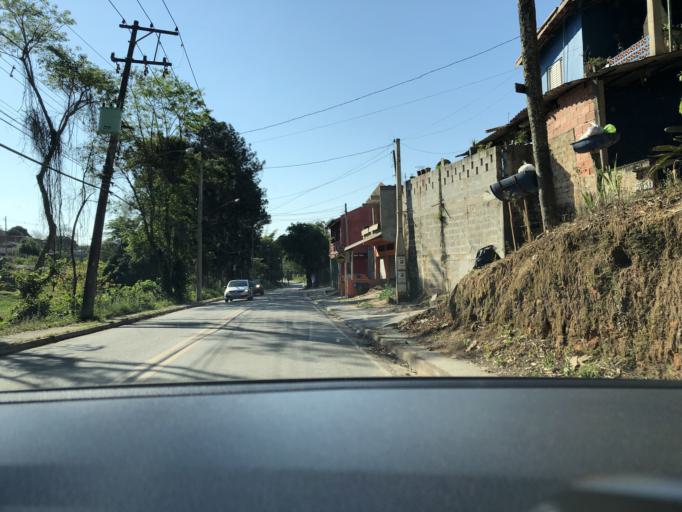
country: BR
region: Sao Paulo
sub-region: Campo Limpo Paulista
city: Campo Limpo Paulista
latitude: -23.1822
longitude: -46.8050
